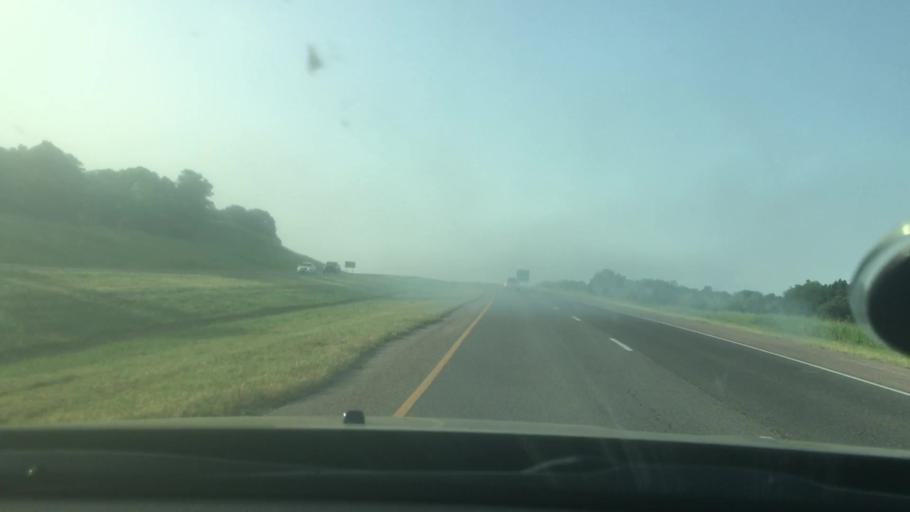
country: US
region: Oklahoma
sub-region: Pontotoc County
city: Ada
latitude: 34.7326
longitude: -96.6410
